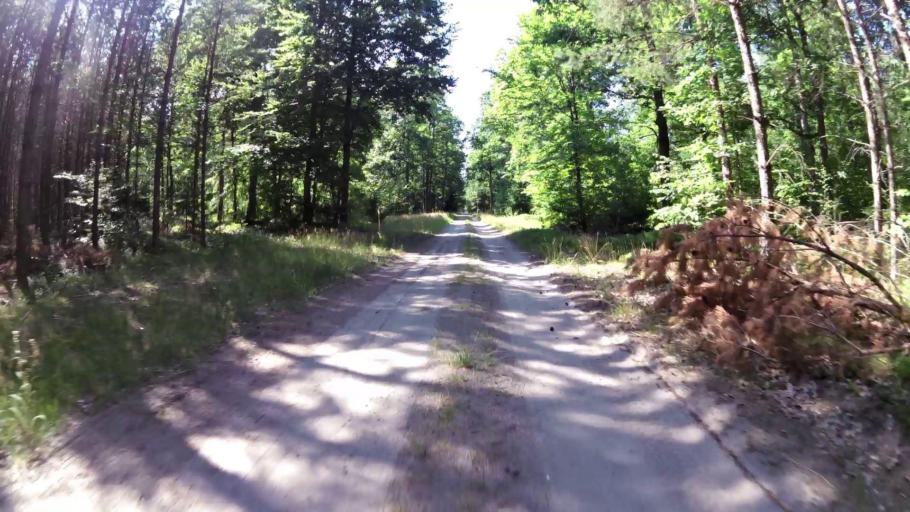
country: PL
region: West Pomeranian Voivodeship
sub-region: Powiat drawski
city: Czaplinek
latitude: 53.4159
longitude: 16.2587
